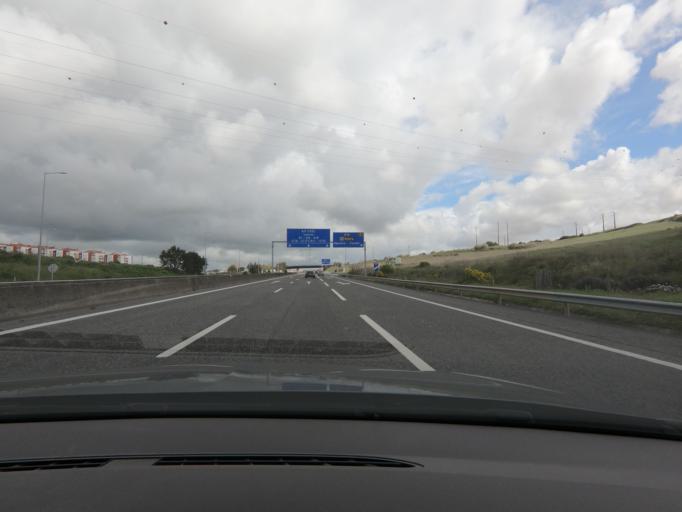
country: PT
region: Lisbon
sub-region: Sintra
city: Belas
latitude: 38.7632
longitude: -9.2699
